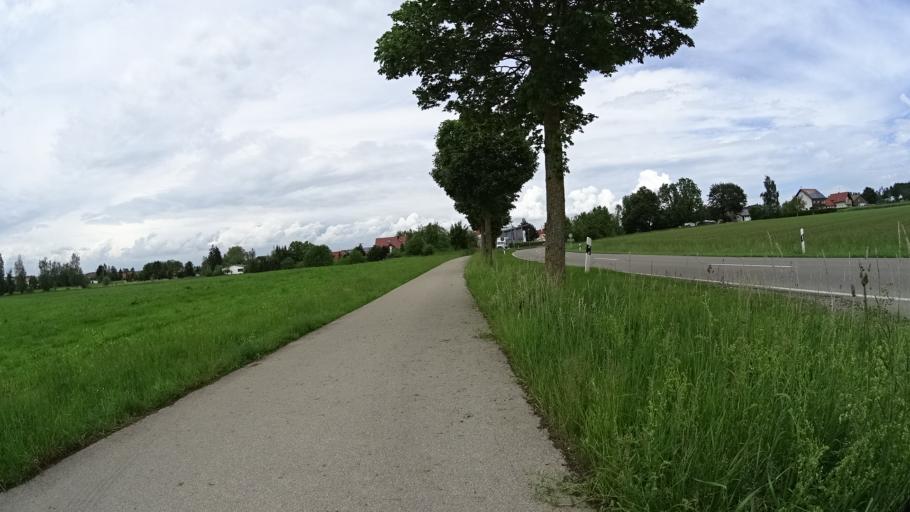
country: DE
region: Bavaria
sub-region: Swabia
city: Pfaffenhofen an der Roth
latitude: 48.3428
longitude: 10.1601
